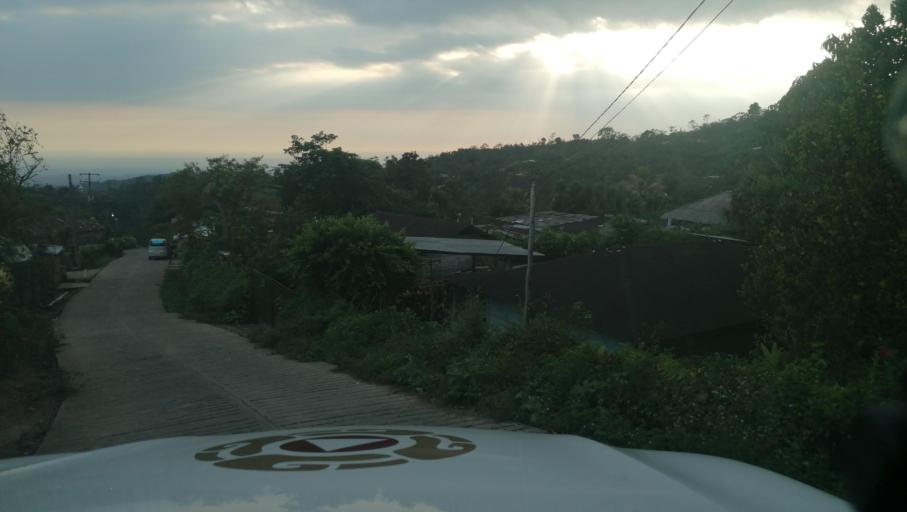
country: MX
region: Chiapas
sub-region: Cacahoatan
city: Benito Juarez
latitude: 15.1041
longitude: -92.2162
